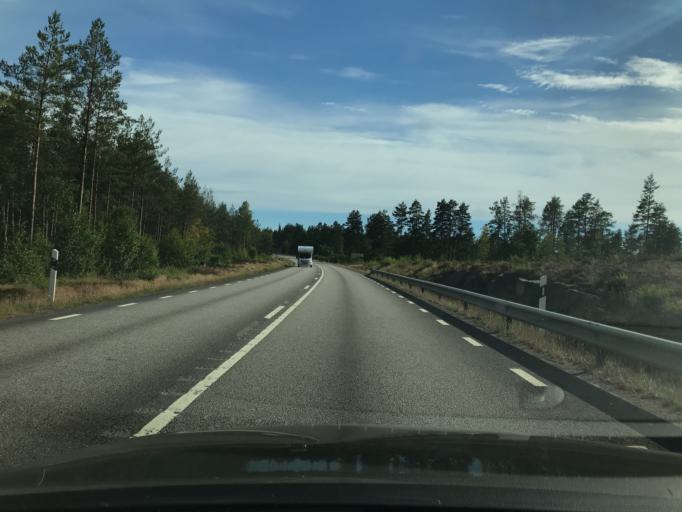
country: SE
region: Kalmar
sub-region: Hultsfreds Kommun
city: Malilla
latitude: 57.4316
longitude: 15.8290
